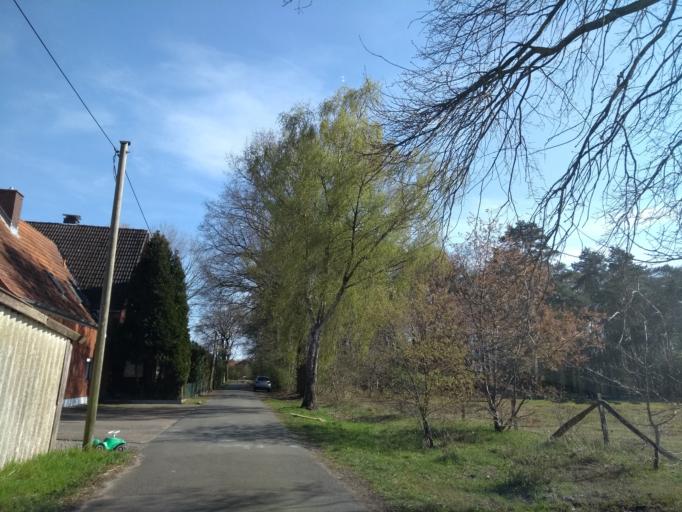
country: DE
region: North Rhine-Westphalia
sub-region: Regierungsbezirk Detmold
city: Hovelhof
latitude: 51.7871
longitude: 8.7149
